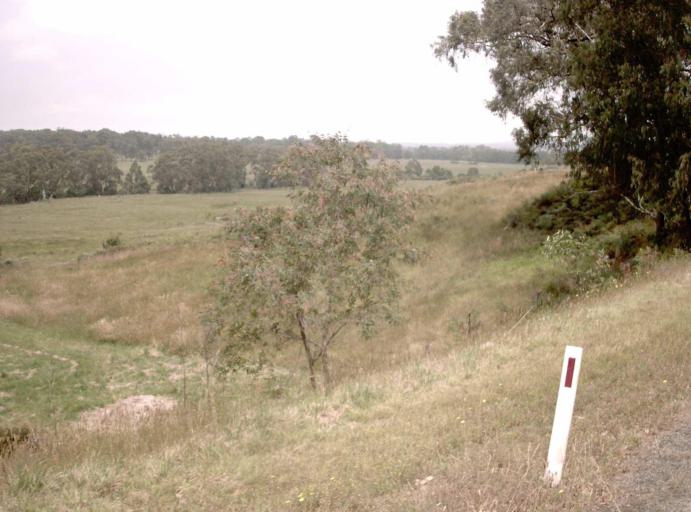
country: AU
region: Victoria
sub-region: Latrobe
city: Traralgon
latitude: -38.4601
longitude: 146.7270
